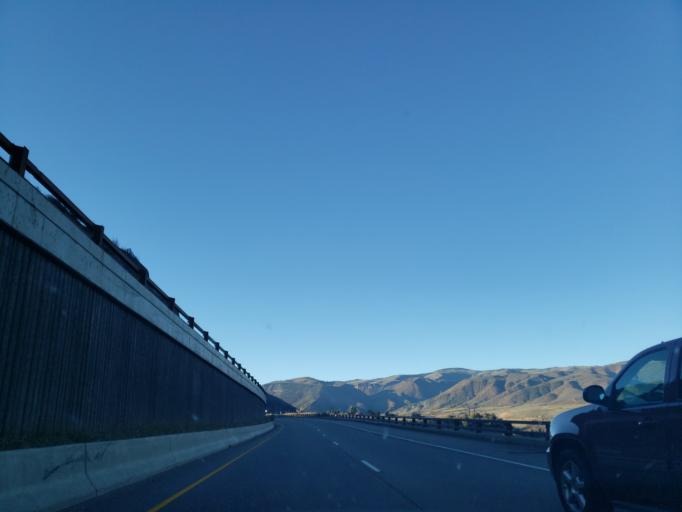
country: US
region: Colorado
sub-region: Pitkin County
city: Snowmass Village
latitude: 39.2444
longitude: -106.8814
